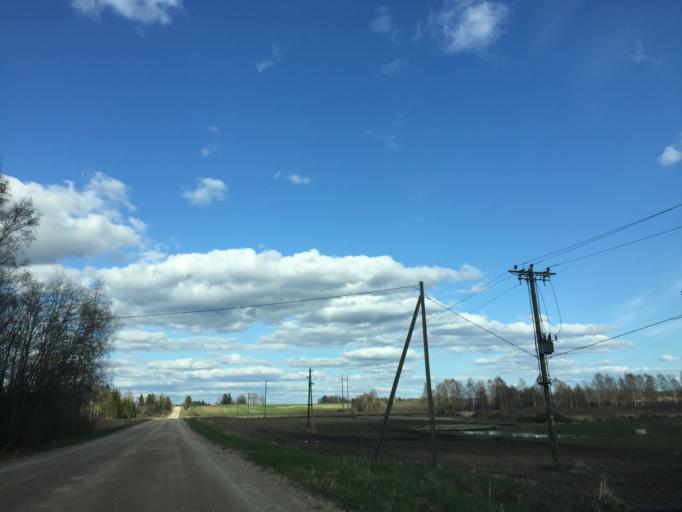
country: LV
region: Rezekne
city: Rezekne
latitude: 56.6435
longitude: 27.3303
